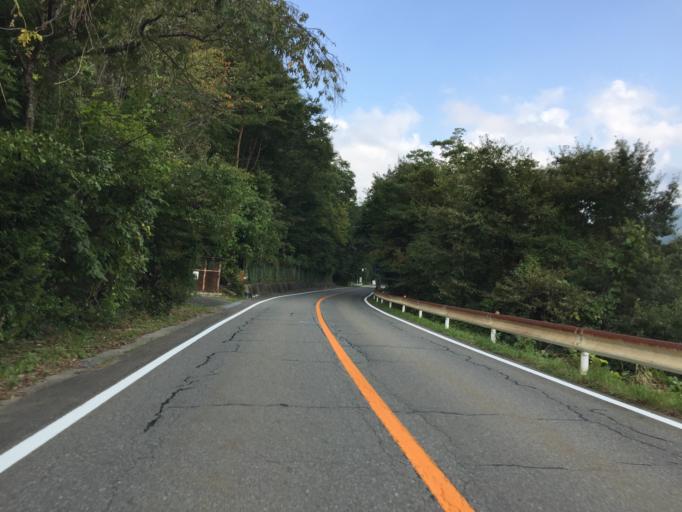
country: JP
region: Fukushima
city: Funehikimachi-funehiki
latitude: 37.5685
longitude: 140.7403
